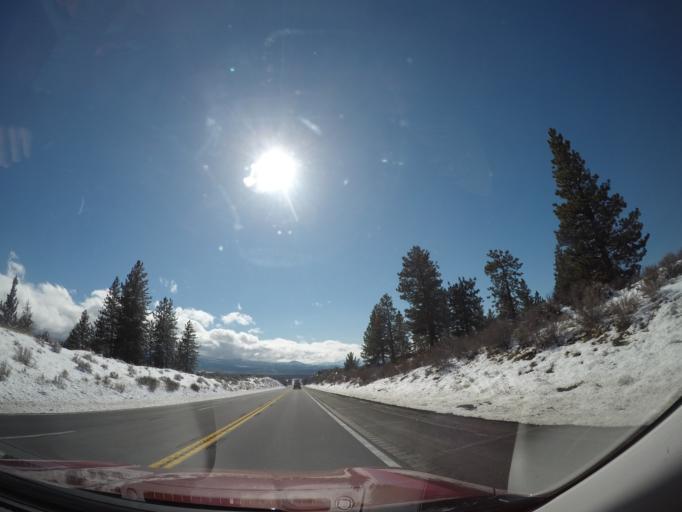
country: US
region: California
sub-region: Siskiyou County
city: Weed
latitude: 41.5694
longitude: -122.1989
